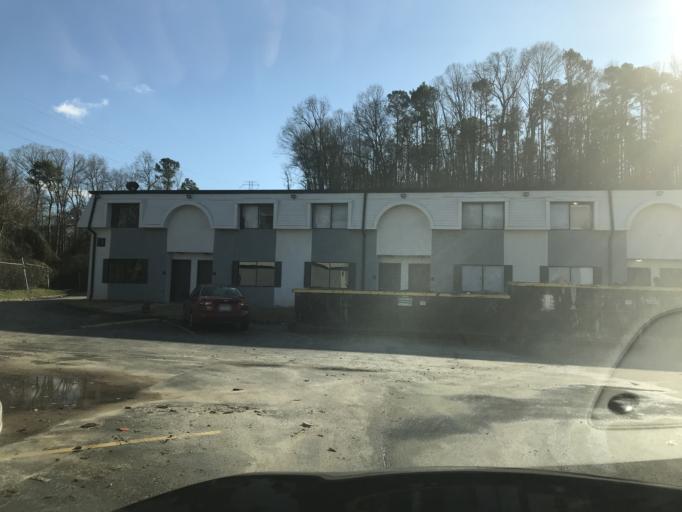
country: US
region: Georgia
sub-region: Fulton County
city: College Park
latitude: 33.6502
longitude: -84.4785
